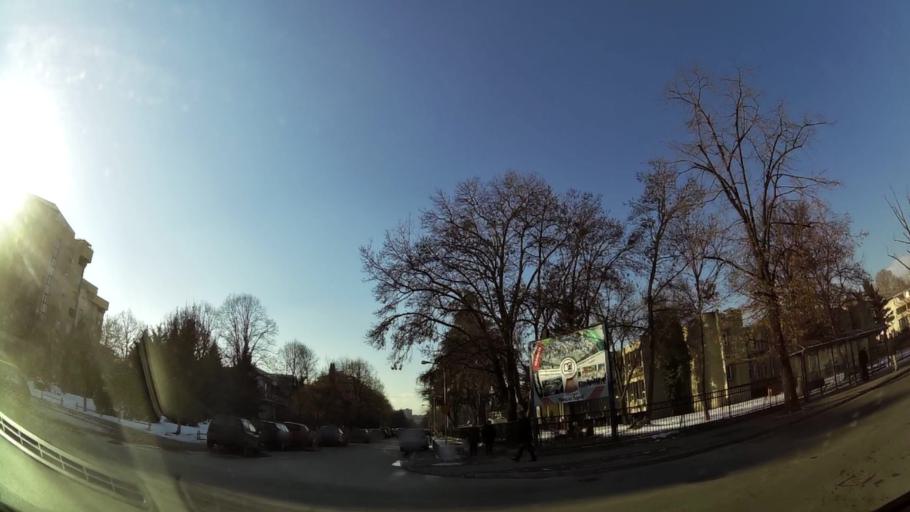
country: MK
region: Karpos
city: Skopje
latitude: 42.0038
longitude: 21.4018
